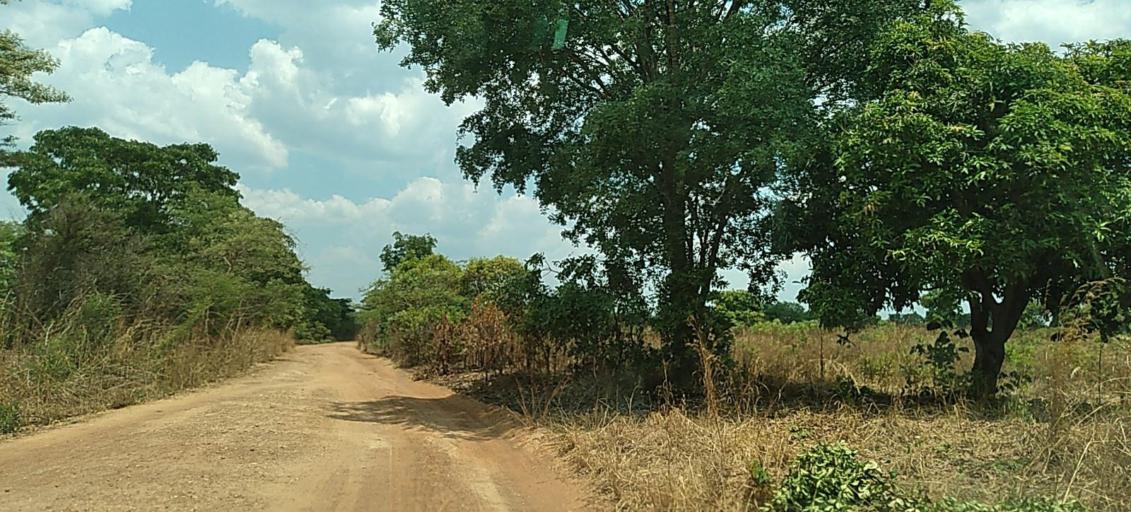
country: ZM
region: Copperbelt
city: Luanshya
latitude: -13.3772
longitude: 28.4297
